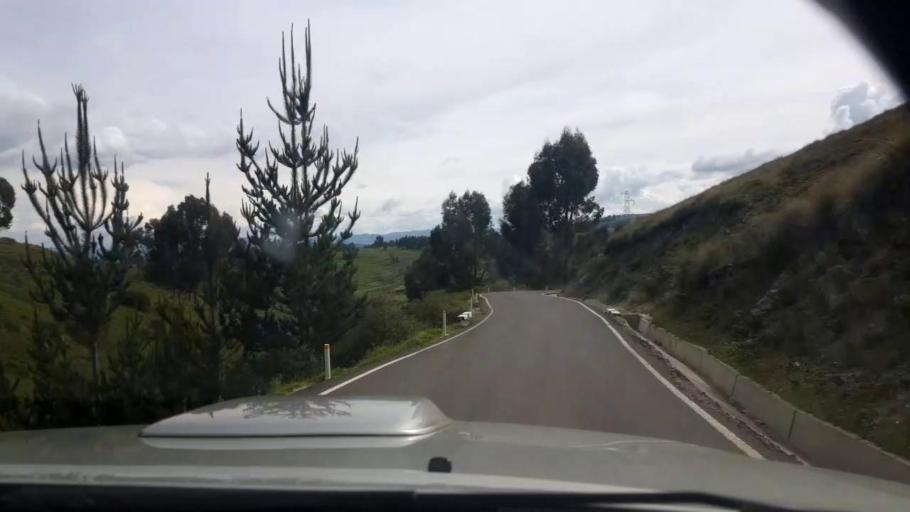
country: PE
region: Ayacucho
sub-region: Provincia de Cangallo
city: Pampa Cangallo
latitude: -13.4490
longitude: -74.1981
